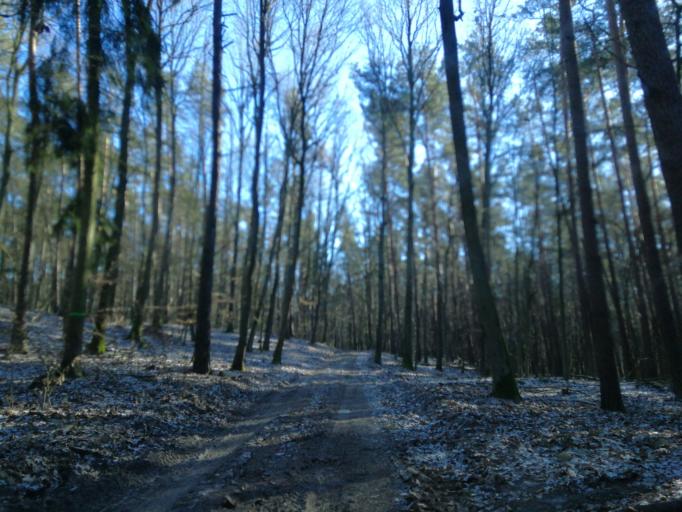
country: PL
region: Kujawsko-Pomorskie
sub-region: Powiat brodnicki
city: Gorzno
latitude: 53.2146
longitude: 19.6756
